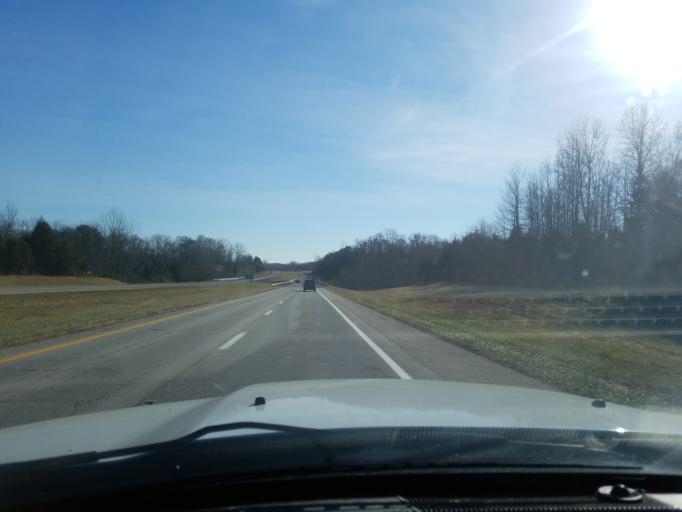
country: US
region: Ohio
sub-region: Brown County
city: Mount Orab
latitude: 39.0236
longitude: -83.8727
